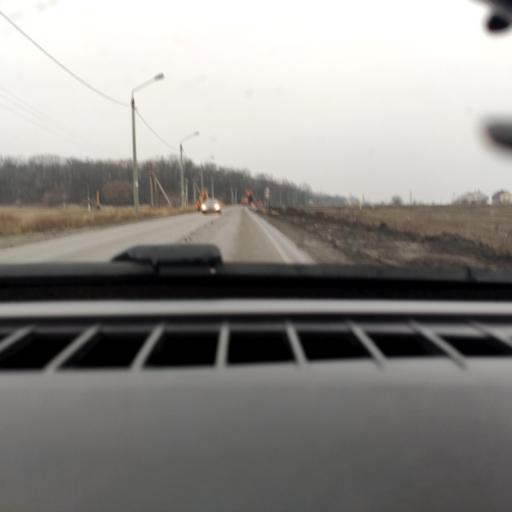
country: RU
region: Voronezj
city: Semiluki
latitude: 51.6550
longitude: 39.0414
